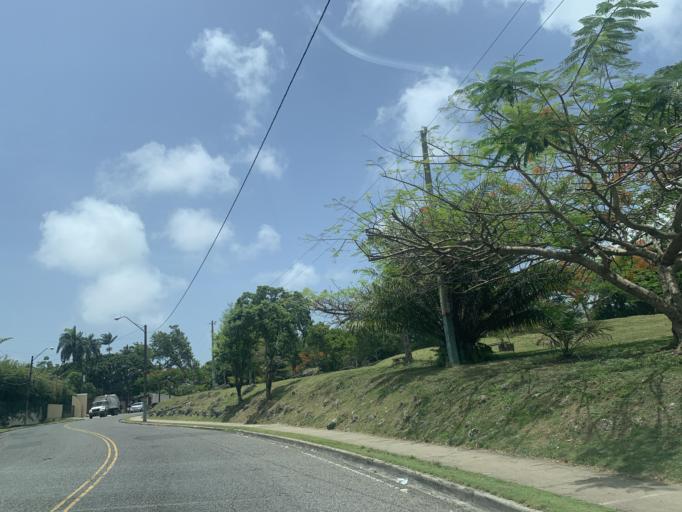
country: DO
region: Nacional
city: La Agustina
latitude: 18.4934
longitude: -69.9490
